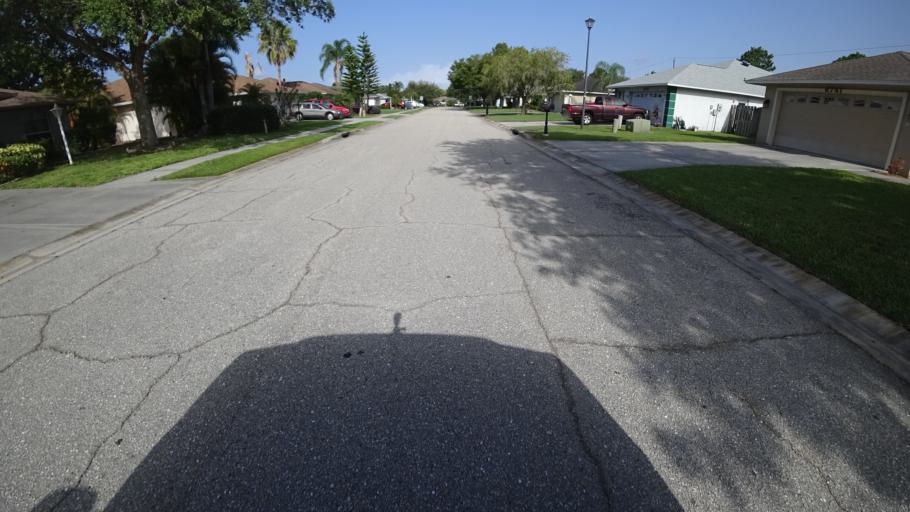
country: US
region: Florida
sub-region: Sarasota County
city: Desoto Lakes
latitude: 27.4247
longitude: -82.4723
